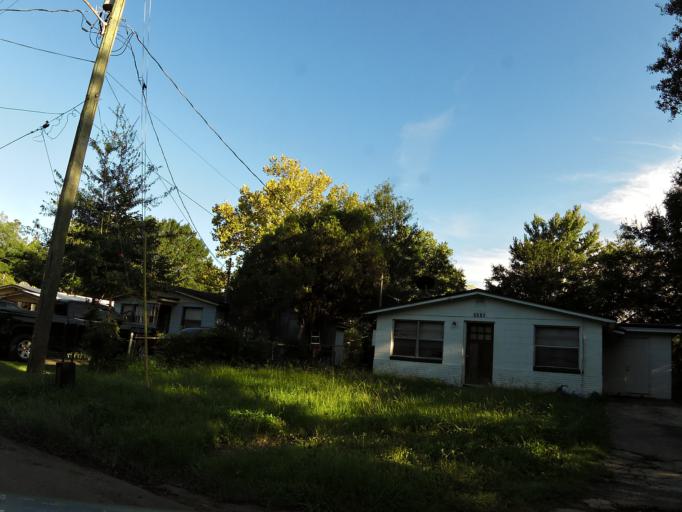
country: US
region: Florida
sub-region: Duval County
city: Jacksonville
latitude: 30.3428
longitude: -81.6955
